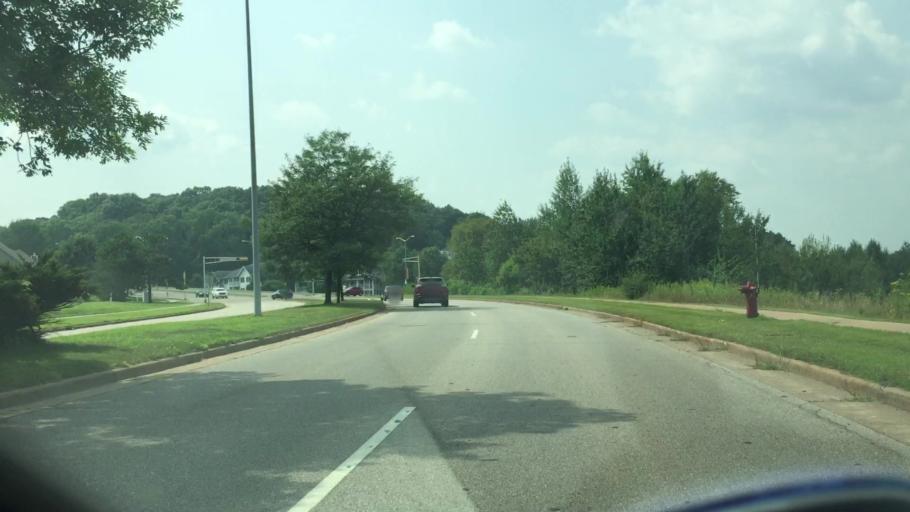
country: US
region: Wisconsin
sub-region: Eau Claire County
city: Altoona
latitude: 44.7718
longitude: -91.4433
